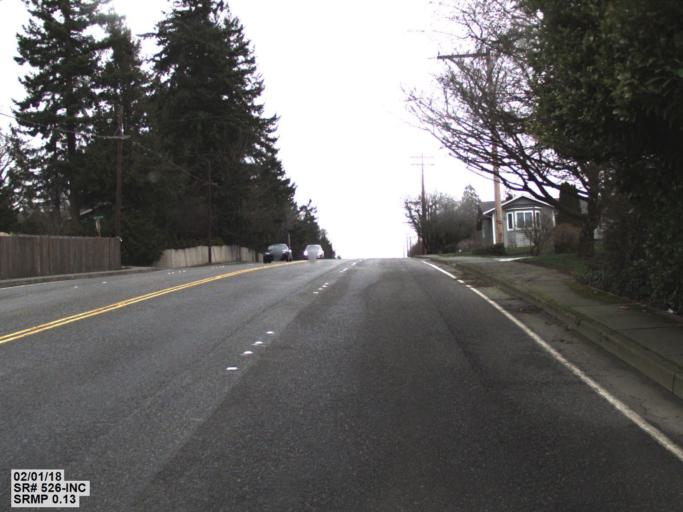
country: US
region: Washington
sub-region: Snohomish County
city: Mukilteo
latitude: 47.9220
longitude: -122.2973
